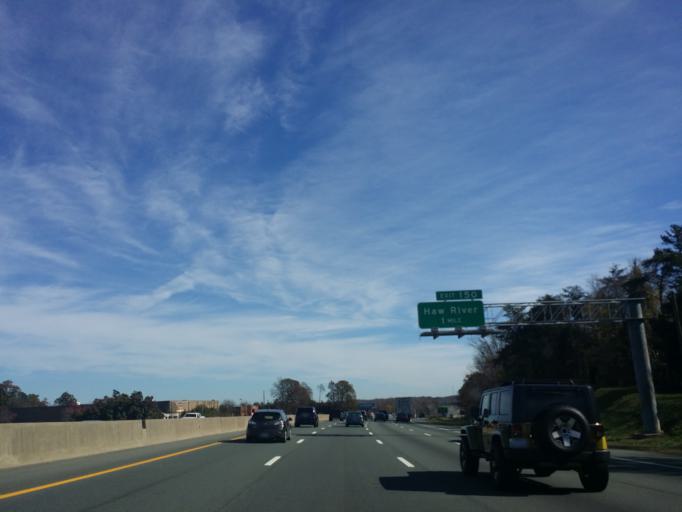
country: US
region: North Carolina
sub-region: Alamance County
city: Haw River
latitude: 36.0684
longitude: -79.3734
